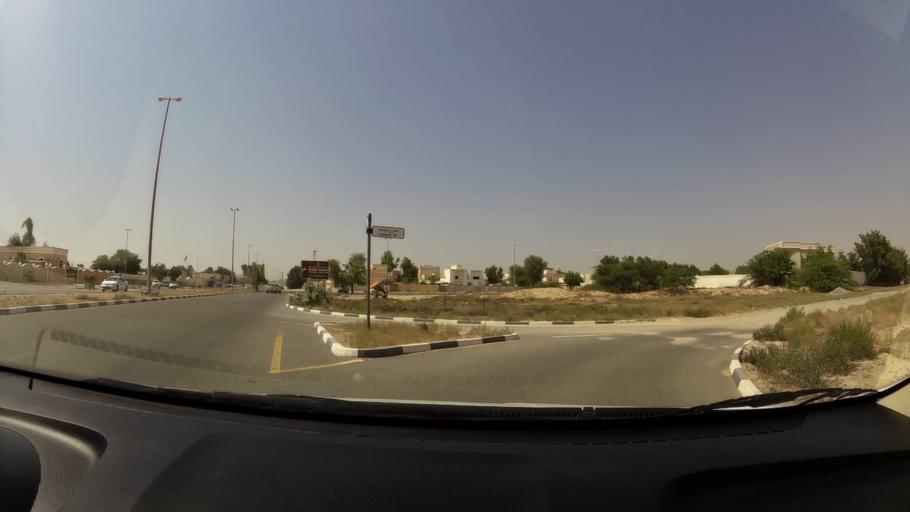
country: AE
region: Umm al Qaywayn
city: Umm al Qaywayn
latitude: 25.4946
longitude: 55.5814
